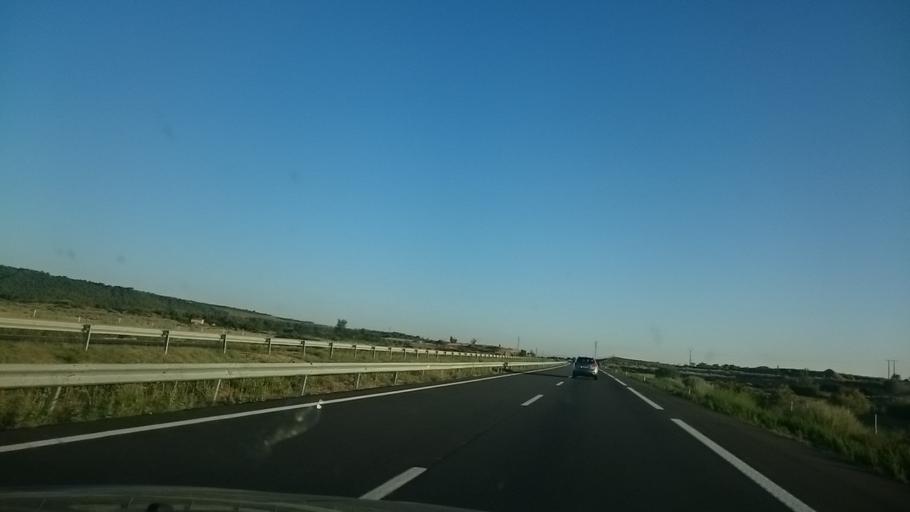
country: ES
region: Navarre
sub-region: Provincia de Navarra
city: Azagra
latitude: 42.2676
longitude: -1.9286
